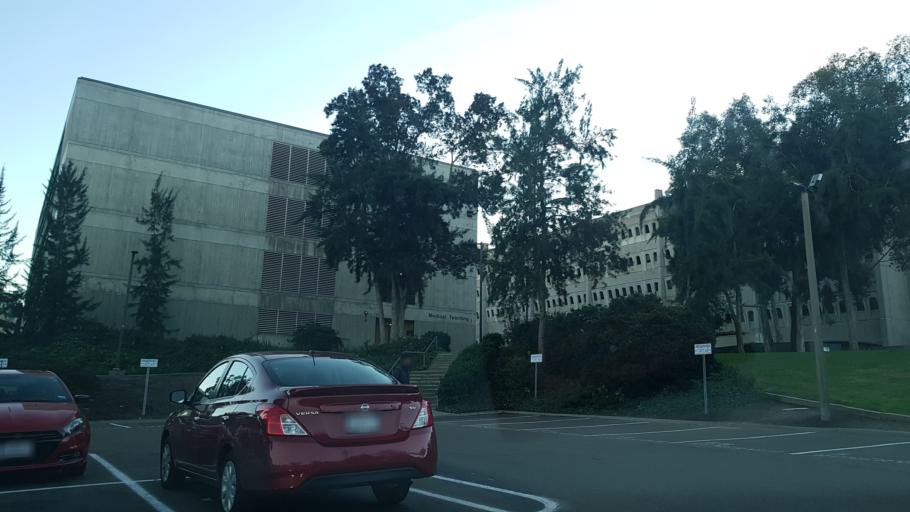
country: US
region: California
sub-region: San Diego County
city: La Jolla
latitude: 32.8767
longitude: -117.2353
